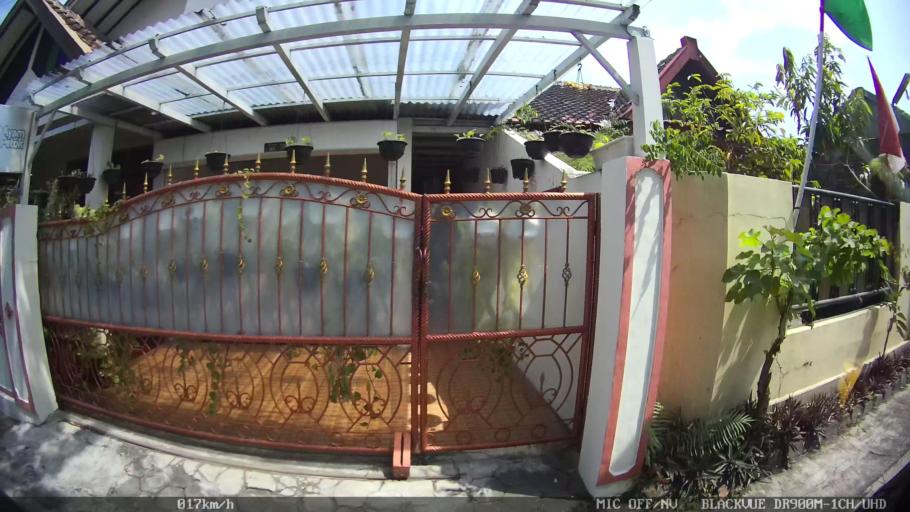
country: ID
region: Daerah Istimewa Yogyakarta
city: Yogyakarta
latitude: -7.8108
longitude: 110.3837
